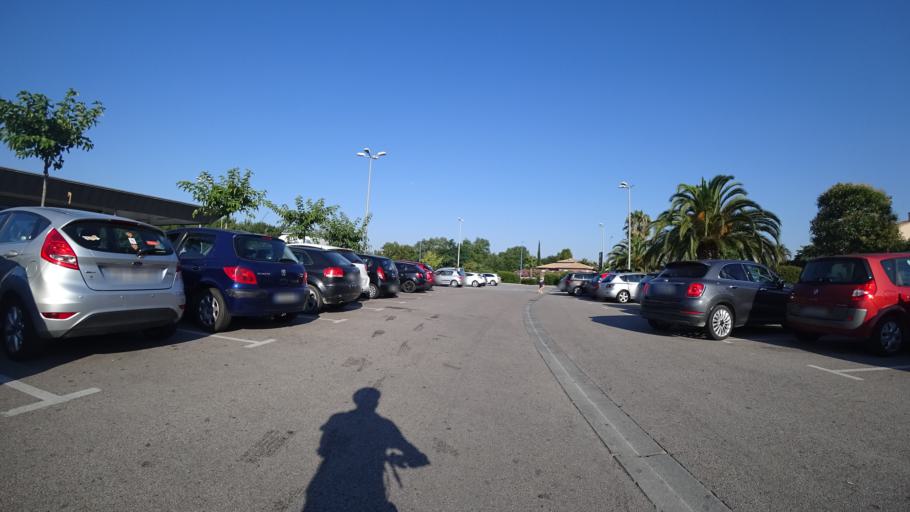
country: FR
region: Languedoc-Roussillon
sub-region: Departement des Pyrenees-Orientales
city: Canet-en-Roussillon
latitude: 42.6996
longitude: 3.0016
